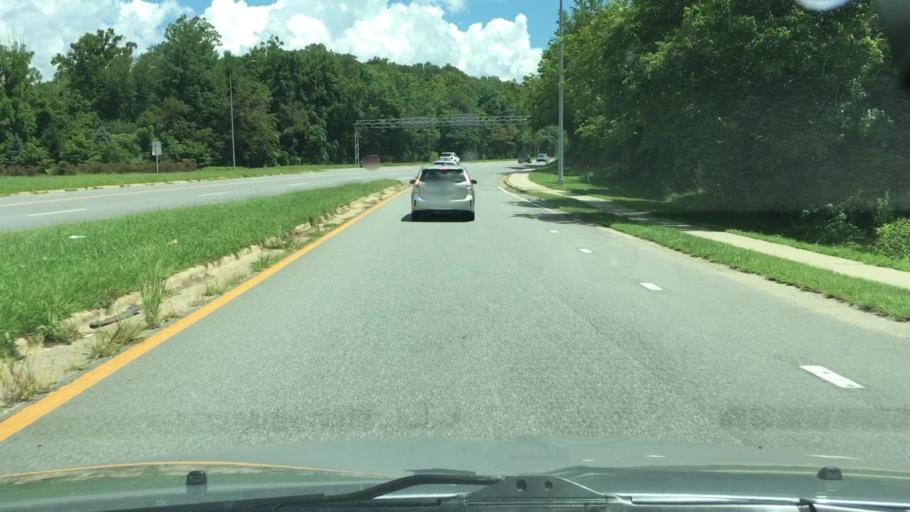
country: US
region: North Carolina
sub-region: Buncombe County
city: Asheville
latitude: 35.5861
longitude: -82.5182
